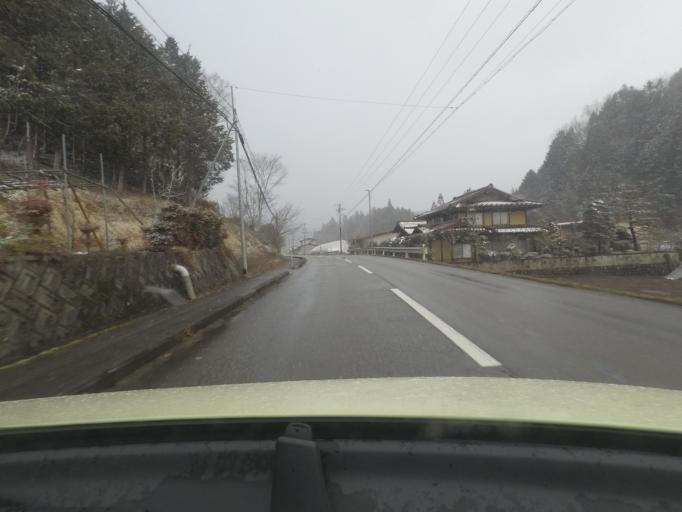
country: JP
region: Gifu
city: Takayama
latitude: 36.1433
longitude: 137.3025
